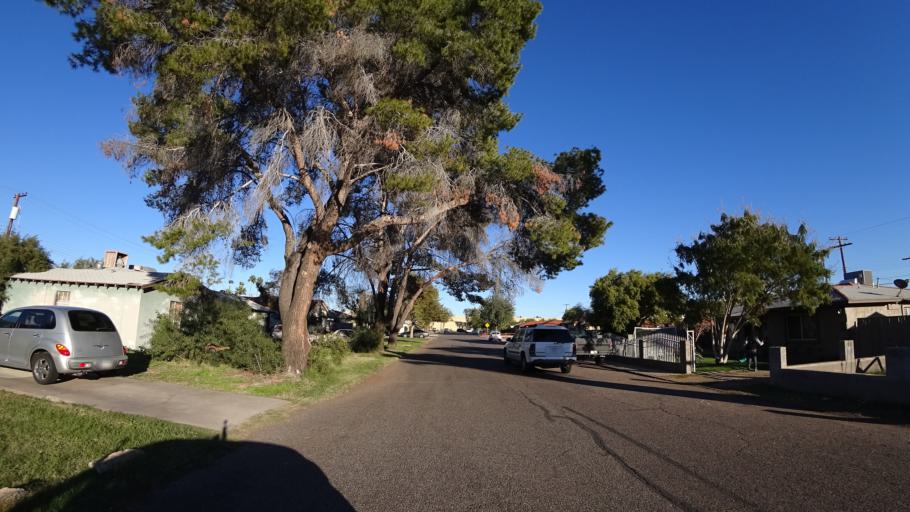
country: US
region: Arizona
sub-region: Maricopa County
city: Phoenix
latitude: 33.4825
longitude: -112.0419
